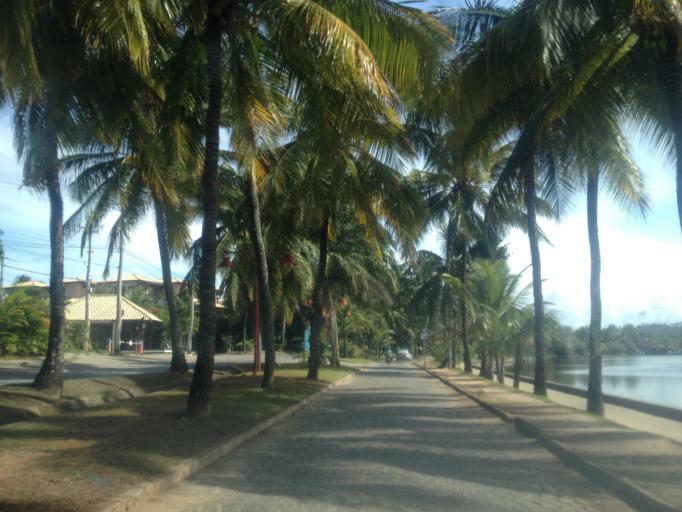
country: BR
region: Bahia
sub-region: Mata De Sao Joao
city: Mata de Sao Joao
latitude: -12.5776
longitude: -38.0100
